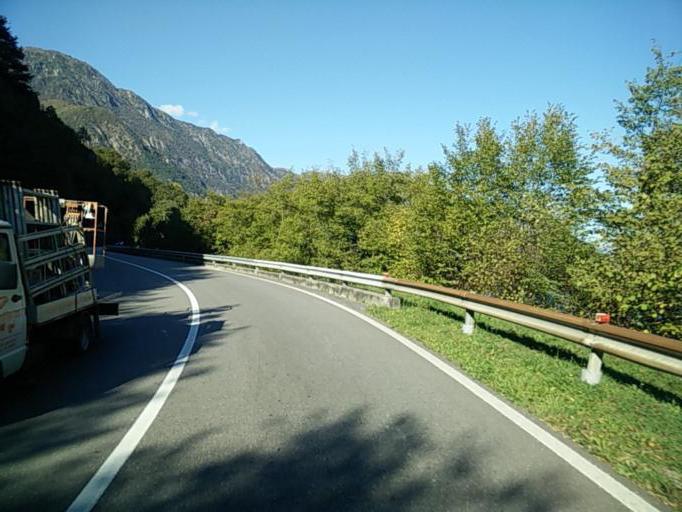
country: IT
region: Lombardy
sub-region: Provincia di Brescia
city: Anfo
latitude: 45.7764
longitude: 10.5038
